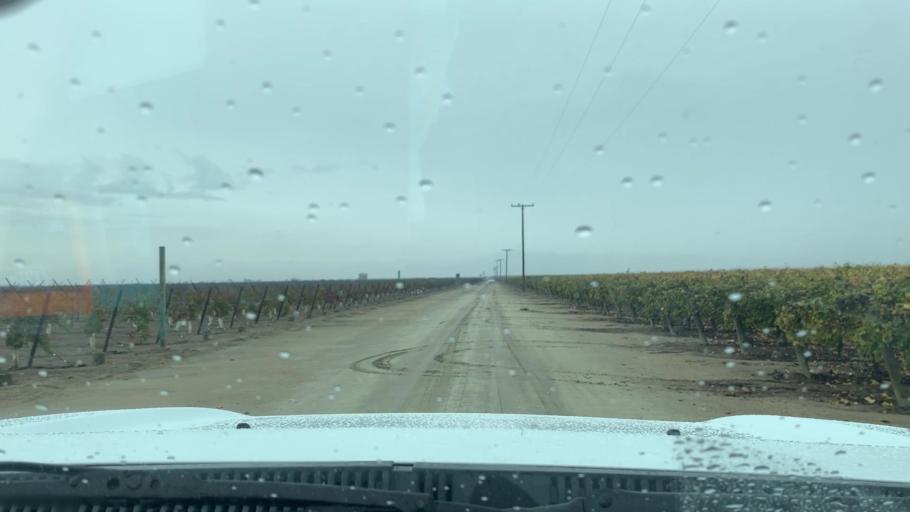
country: US
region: California
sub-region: Tulare County
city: Richgrove
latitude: 35.8345
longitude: -119.1701
